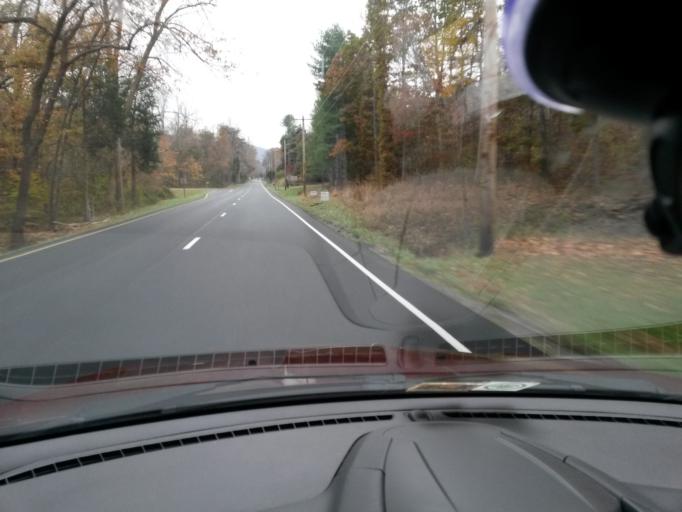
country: US
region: Virginia
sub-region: Albemarle County
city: Crozet
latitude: 37.9389
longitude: -78.6699
